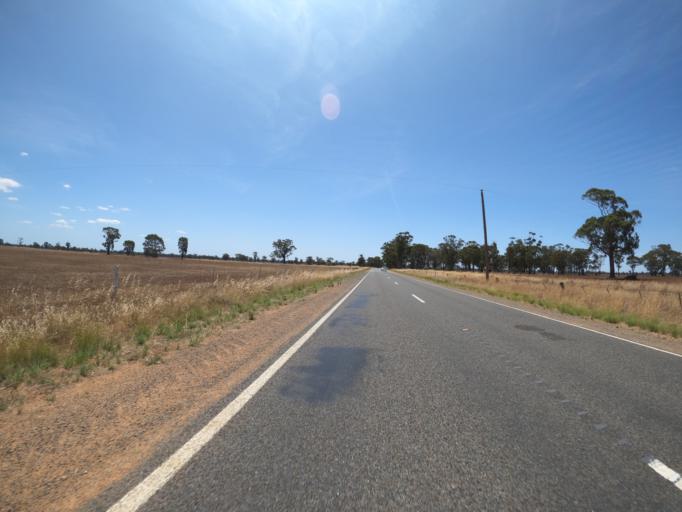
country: AU
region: Victoria
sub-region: Moira
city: Yarrawonga
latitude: -36.2006
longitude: 145.9672
